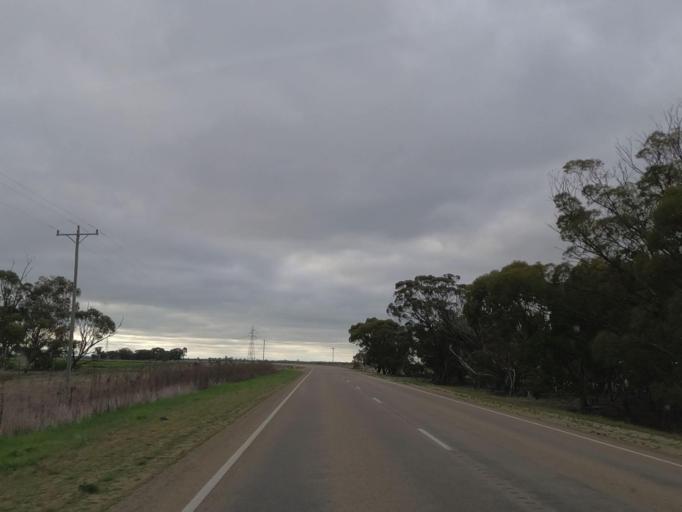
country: AU
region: Victoria
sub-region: Swan Hill
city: Swan Hill
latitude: -35.9101
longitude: 143.9462
